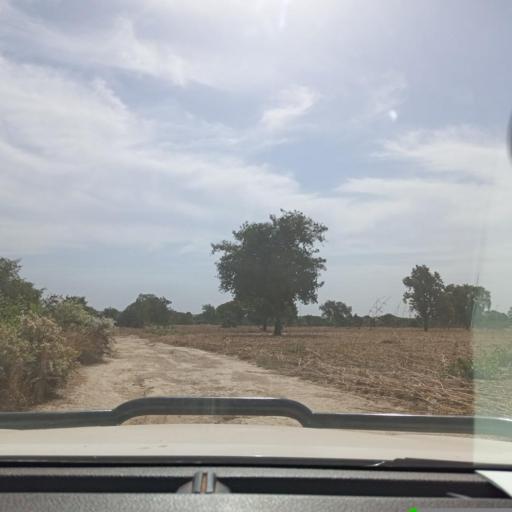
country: ML
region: Koulikoro
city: Kati
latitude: 12.7306
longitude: -8.2542
